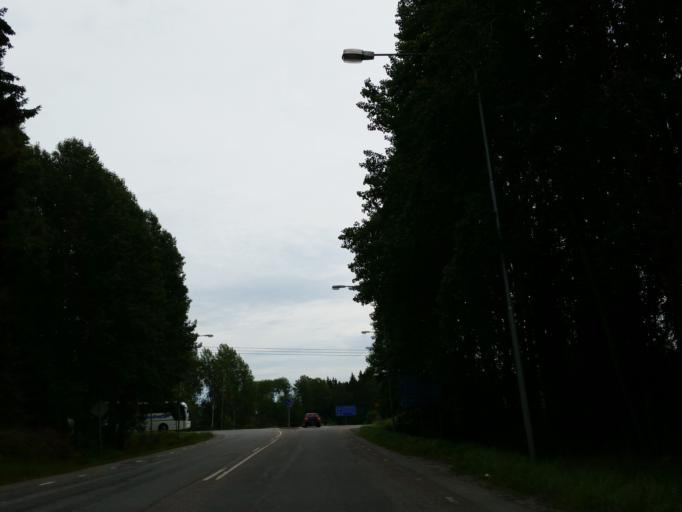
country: SE
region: Stockholm
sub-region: Nykvarns Kommun
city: Nykvarn
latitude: 59.1740
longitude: 17.4506
